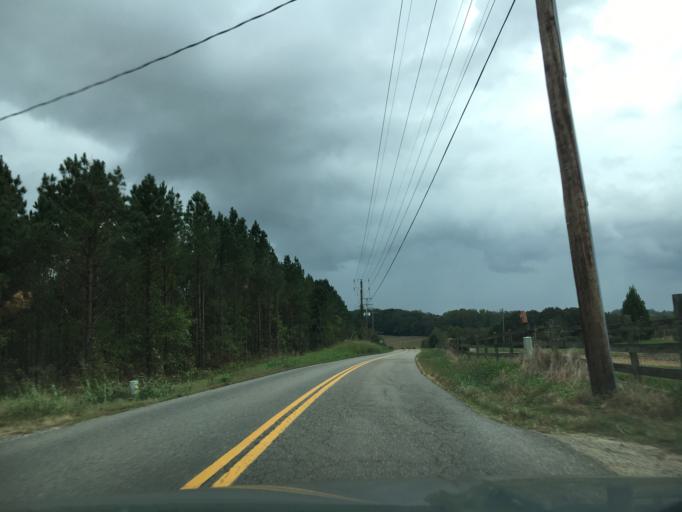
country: US
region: Virginia
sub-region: Amelia County
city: Amelia Court House
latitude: 37.3812
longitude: -77.9787
